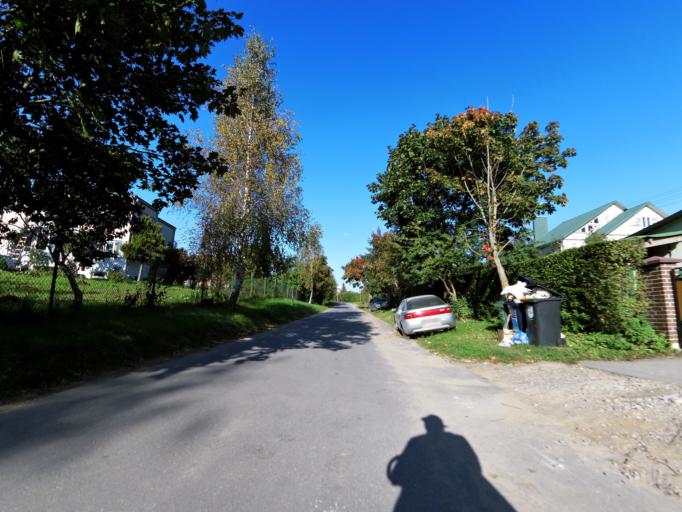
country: LT
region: Vilnius County
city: Pilaite
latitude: 54.7226
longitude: 25.1815
